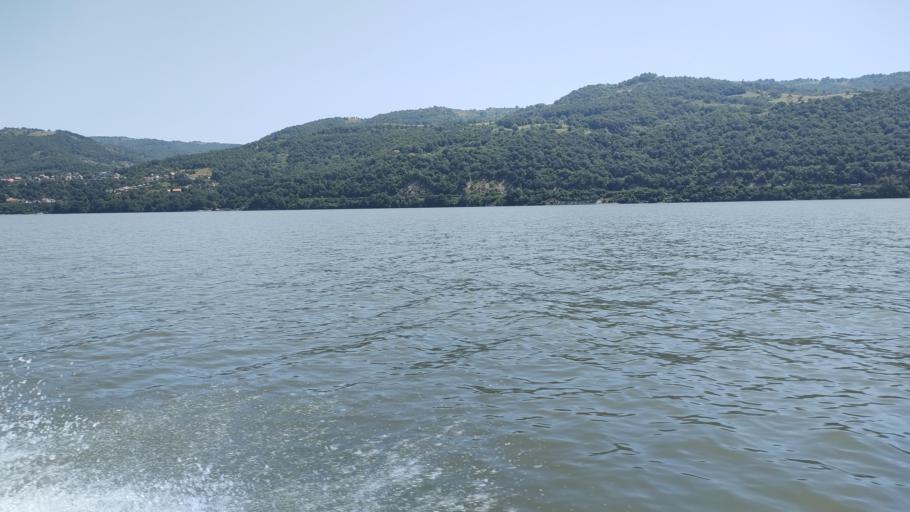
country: RO
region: Mehedinti
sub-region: Comuna Svinita
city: Svinita
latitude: 44.4894
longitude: 22.1846
